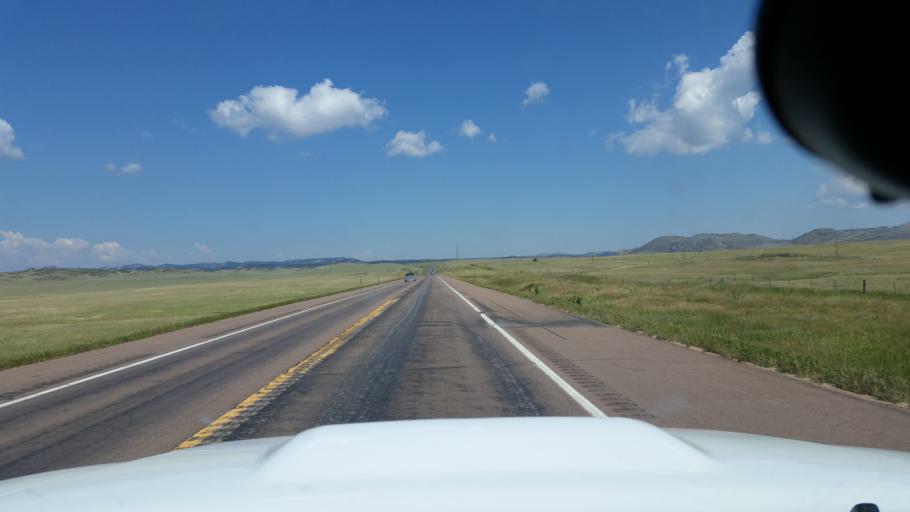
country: US
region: Colorado
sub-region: Larimer County
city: Laporte
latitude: 40.9138
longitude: -105.3183
